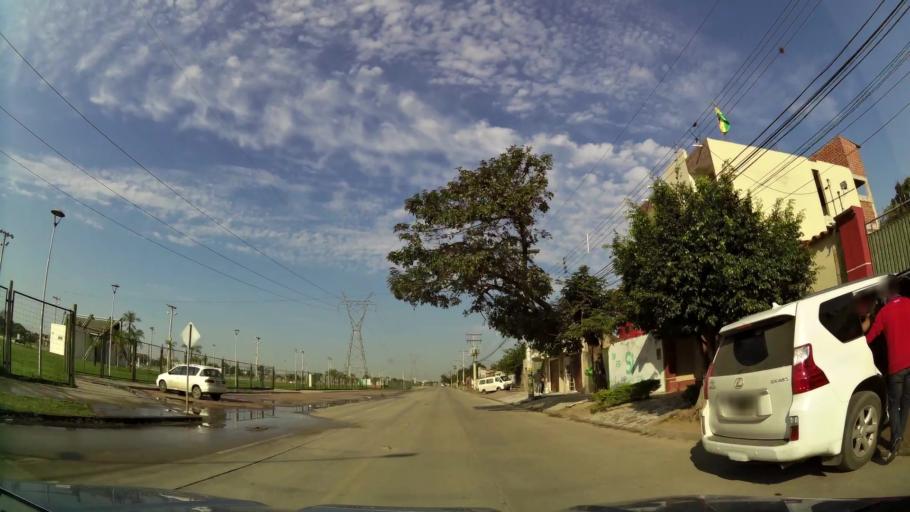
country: BO
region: Santa Cruz
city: Santa Cruz de la Sierra
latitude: -17.7430
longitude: -63.1470
